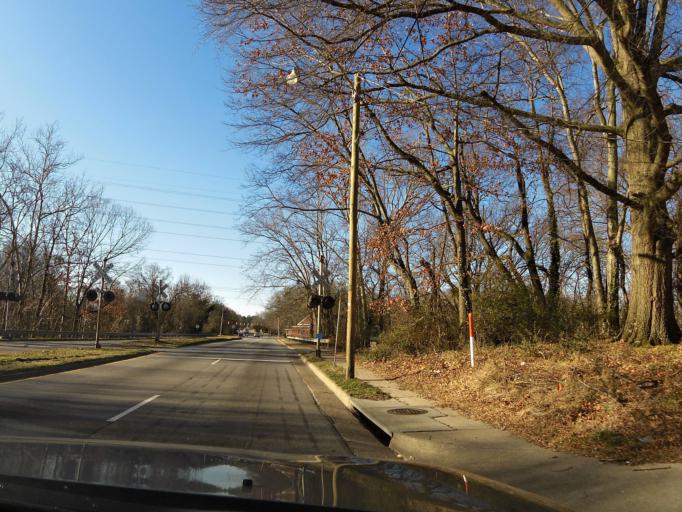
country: US
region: Virginia
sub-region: City of Hopewell
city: Hopewell
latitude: 37.2890
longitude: -77.2954
